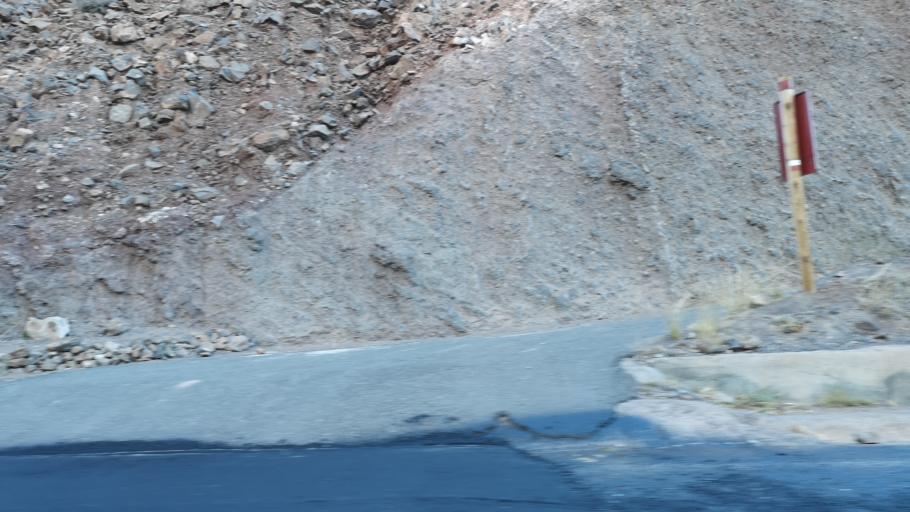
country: ES
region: Canary Islands
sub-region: Provincia de Santa Cruz de Tenerife
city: Alajero
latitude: 28.0341
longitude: -17.2028
